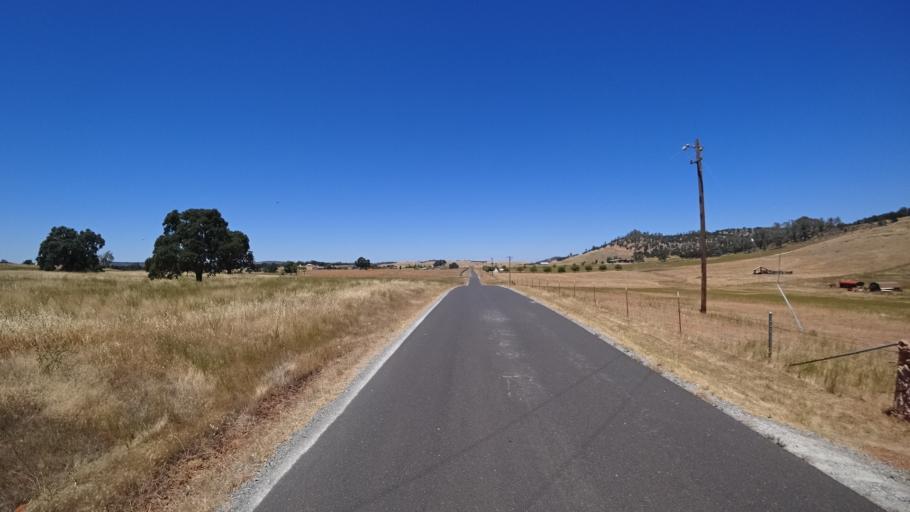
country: US
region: California
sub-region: Calaveras County
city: Copperopolis
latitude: 37.9777
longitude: -120.6626
